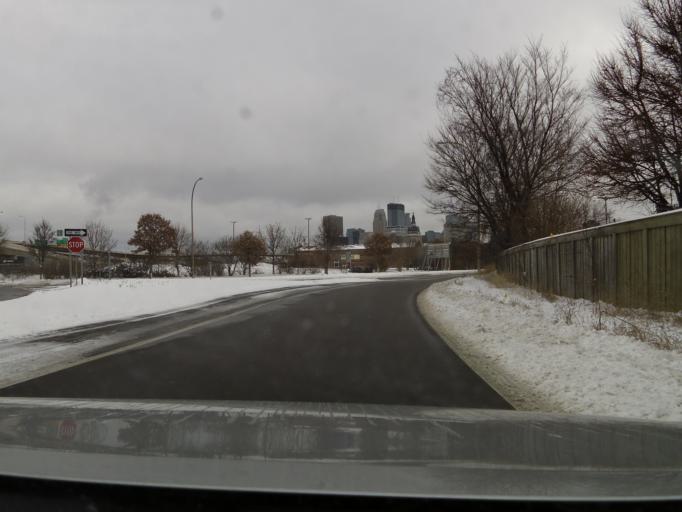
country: US
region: Minnesota
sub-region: Hennepin County
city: Minneapolis
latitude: 44.9720
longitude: -93.2947
